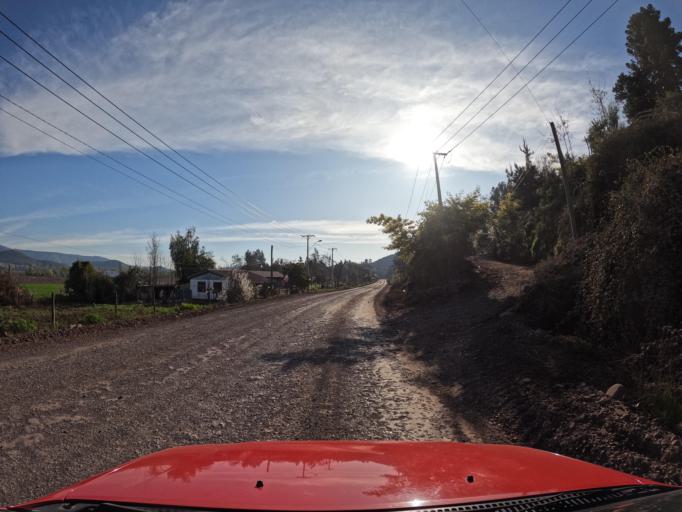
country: CL
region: Maule
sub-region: Provincia de Curico
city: Teno
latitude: -34.9698
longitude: -70.9370
